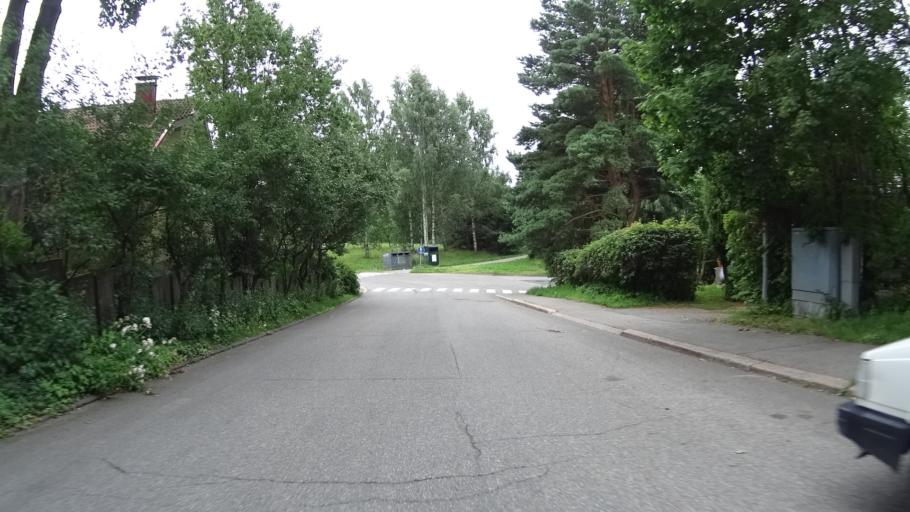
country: FI
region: Uusimaa
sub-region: Helsinki
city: Teekkarikylae
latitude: 60.2316
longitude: 24.8447
